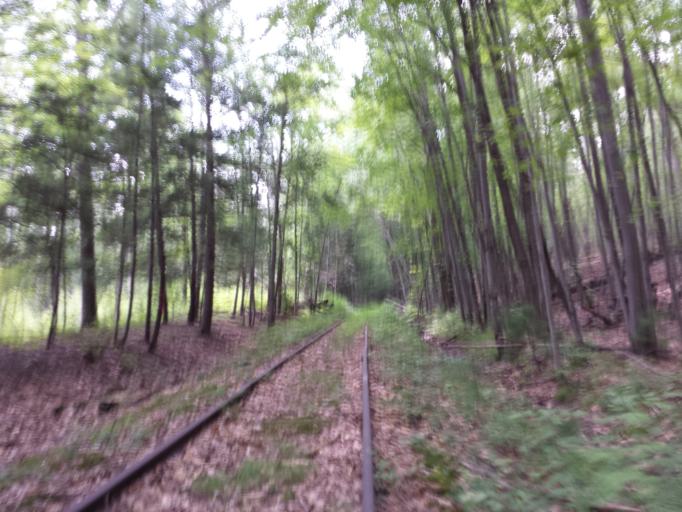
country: US
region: New York
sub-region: Ulster County
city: Shokan
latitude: 41.9671
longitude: -74.2245
